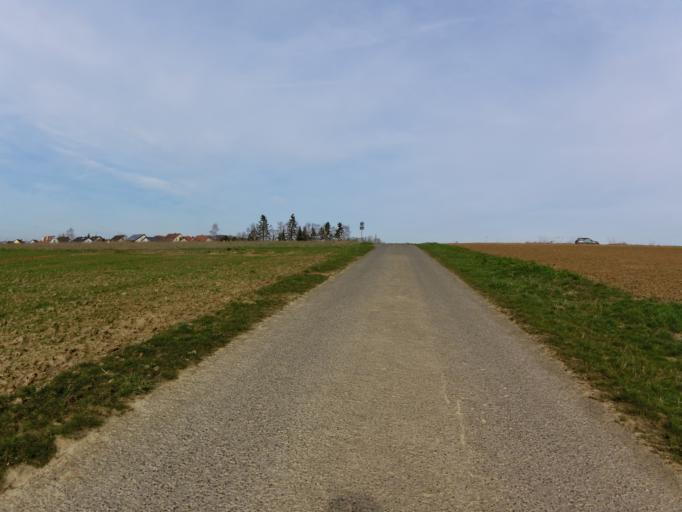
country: DE
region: Bavaria
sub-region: Regierungsbezirk Unterfranken
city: Biebelried
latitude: 49.7618
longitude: 10.0907
